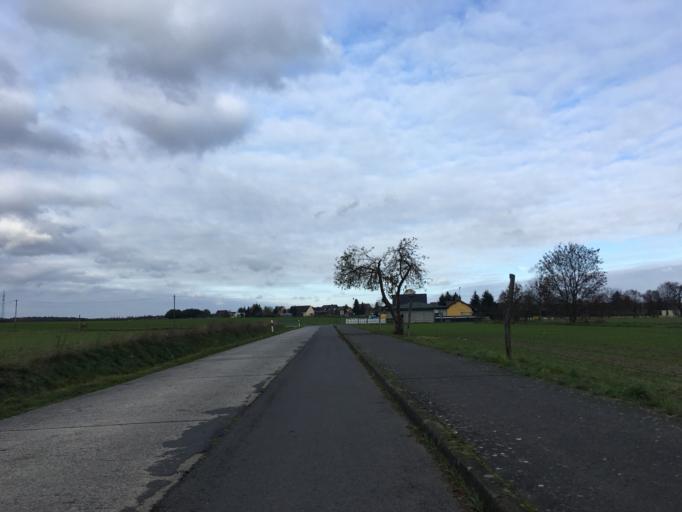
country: DE
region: Brandenburg
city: Schenkendobern
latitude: 51.9772
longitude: 14.5331
